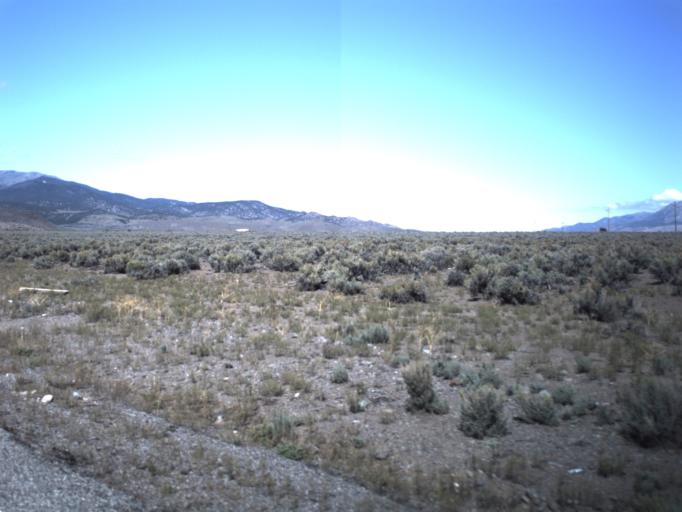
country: US
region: Utah
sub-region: Piute County
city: Junction
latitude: 38.2473
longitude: -112.2360
